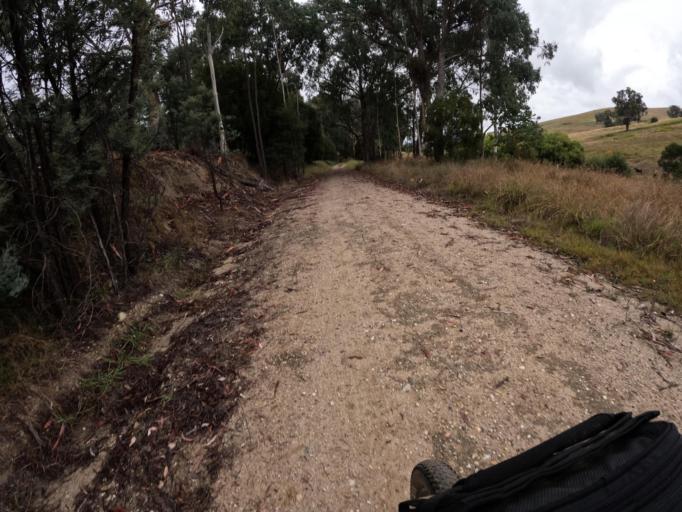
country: AU
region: New South Wales
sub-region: Greater Hume Shire
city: Holbrook
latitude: -36.1592
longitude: 147.4101
